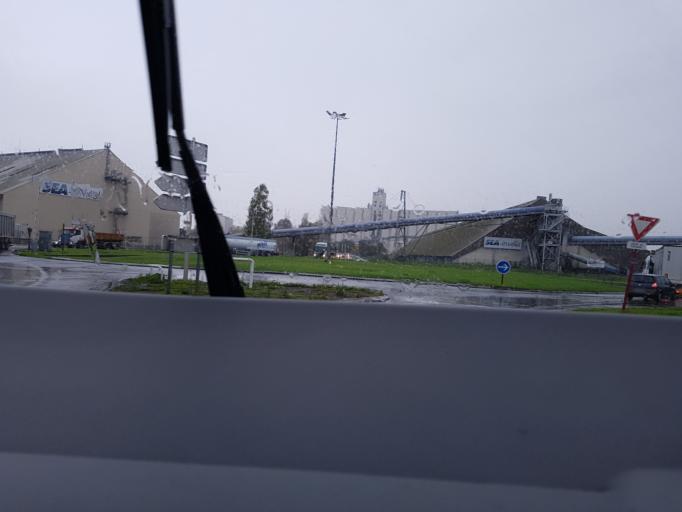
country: FR
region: Aquitaine
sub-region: Departement de la Gironde
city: Bassens
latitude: 44.9087
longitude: -0.5350
